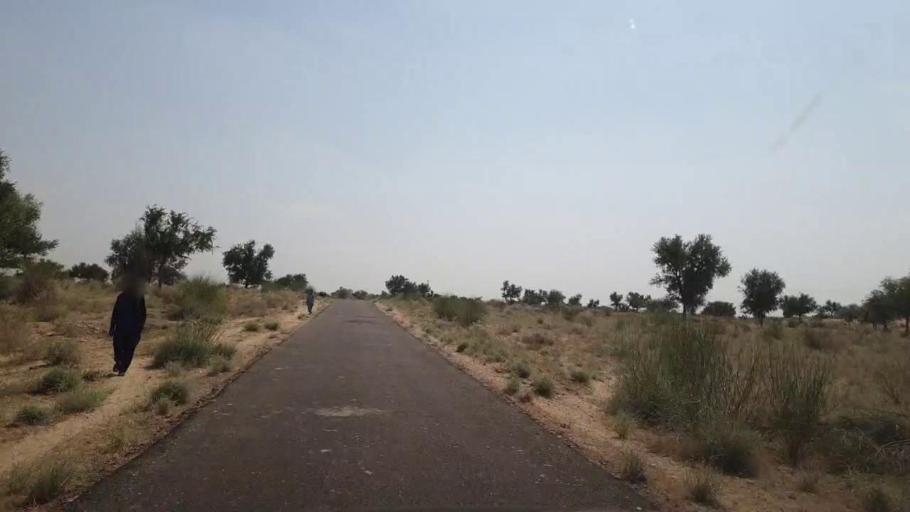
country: PK
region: Sindh
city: Islamkot
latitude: 25.1004
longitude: 70.7259
